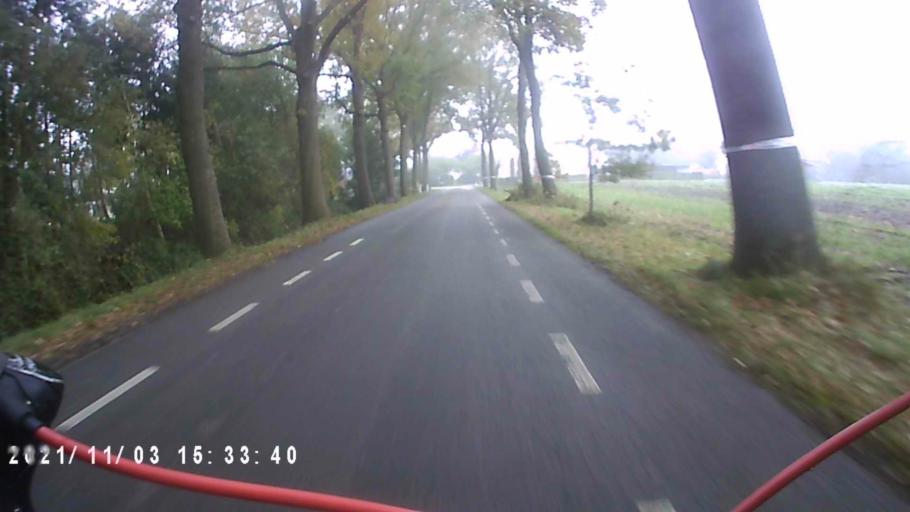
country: NL
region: Groningen
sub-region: Gemeente Leek
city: Leek
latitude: 53.1225
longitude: 6.3646
